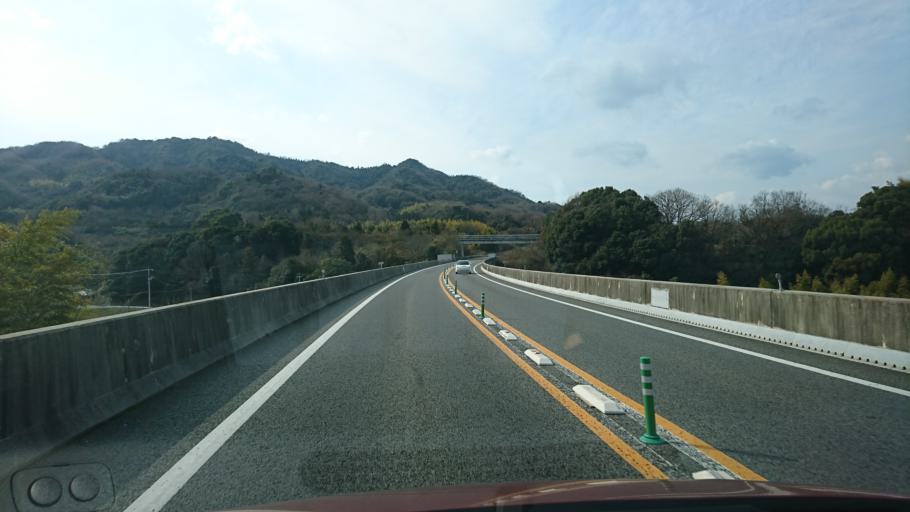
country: JP
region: Hiroshima
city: Innoshima
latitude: 34.1292
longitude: 133.0411
